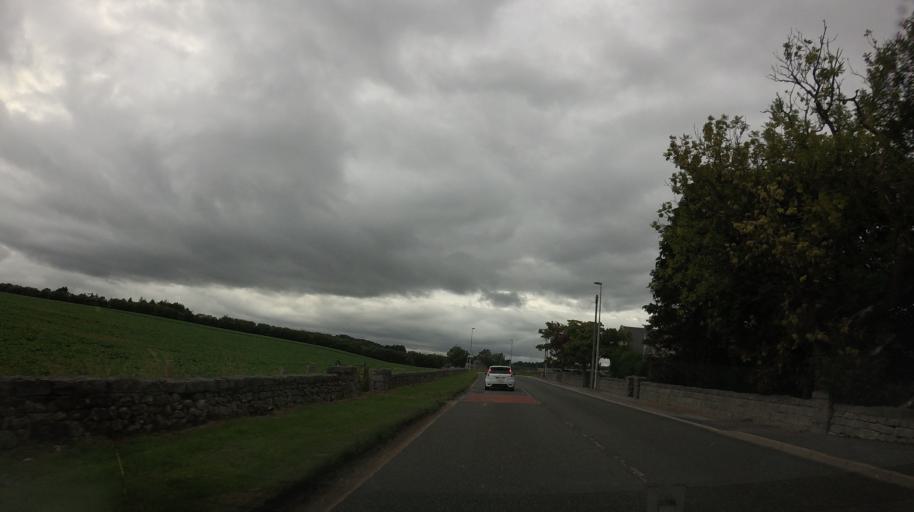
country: GB
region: Scotland
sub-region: Aberdeenshire
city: Kemnay
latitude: 57.1737
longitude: -2.4178
